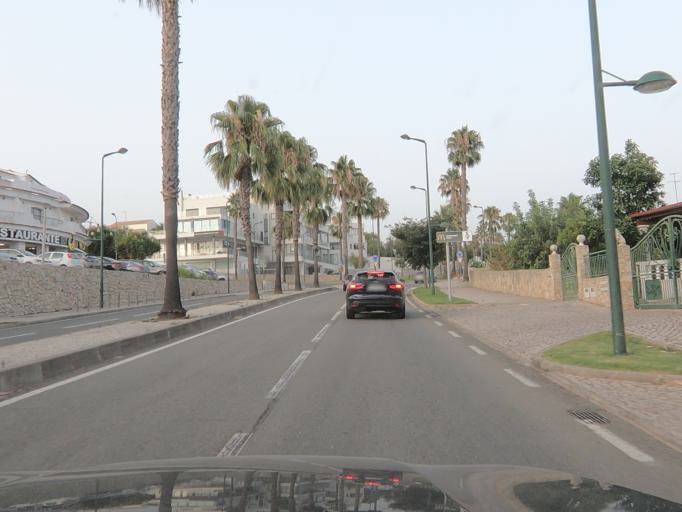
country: PT
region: Faro
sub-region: Loule
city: Loule
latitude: 37.1352
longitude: -8.0330
